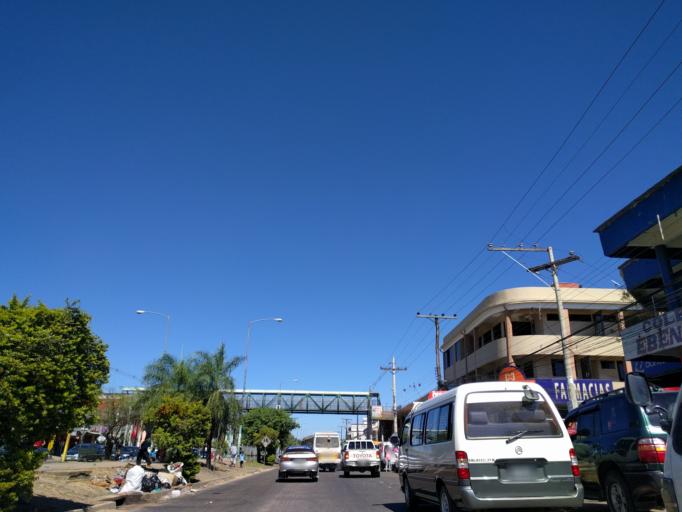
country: BO
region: Santa Cruz
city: Santa Cruz de la Sierra
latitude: -17.8276
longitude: -63.2262
